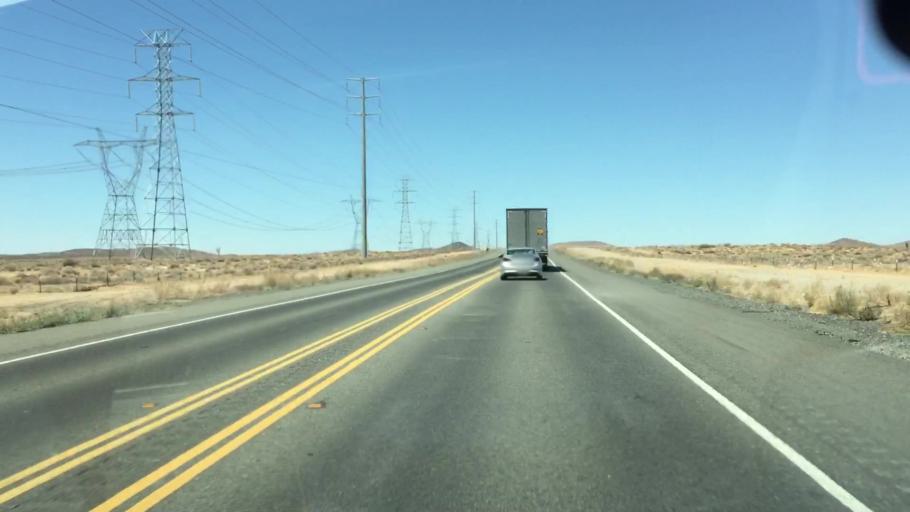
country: US
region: California
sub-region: Kern County
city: Boron
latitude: 34.8157
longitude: -117.4926
